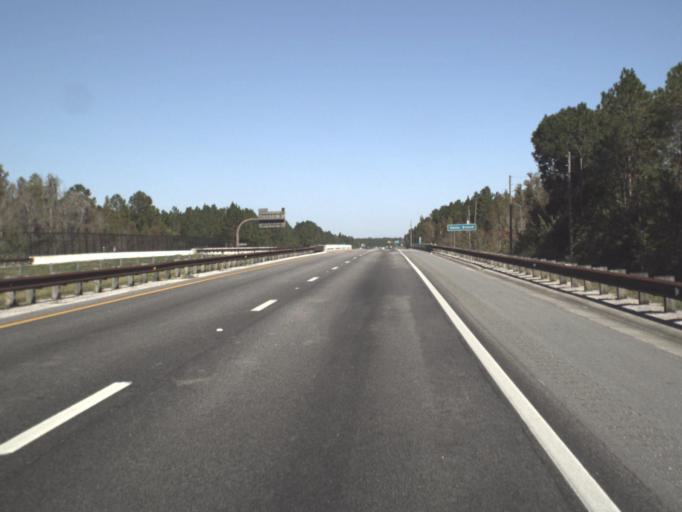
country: US
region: Florida
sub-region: Pasco County
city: Odessa
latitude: 28.2130
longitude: -82.5485
